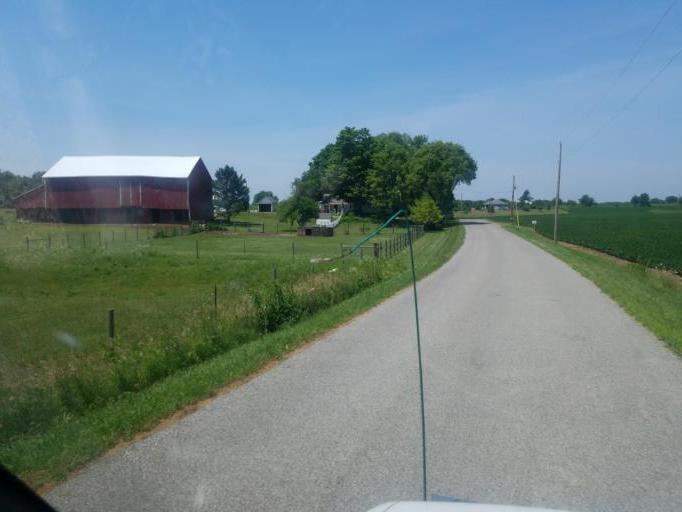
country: US
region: Ohio
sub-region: Logan County
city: West Liberty
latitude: 40.2920
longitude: -83.8235
